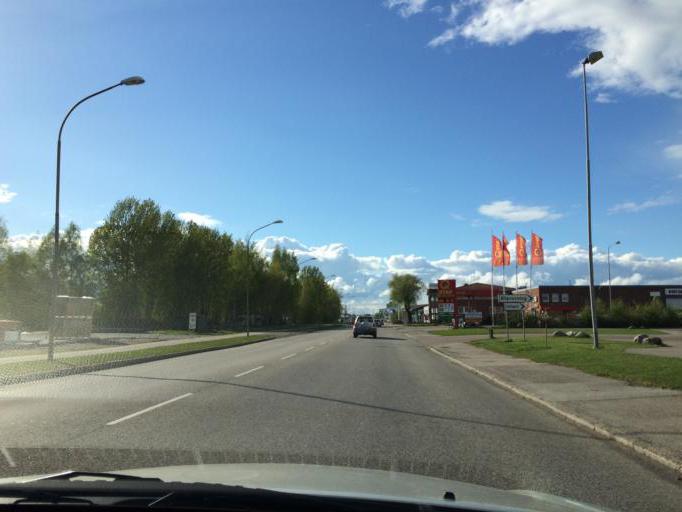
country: SE
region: Soedermanland
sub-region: Eskilstuna Kommun
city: Eskilstuna
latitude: 59.3835
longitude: 16.4945
